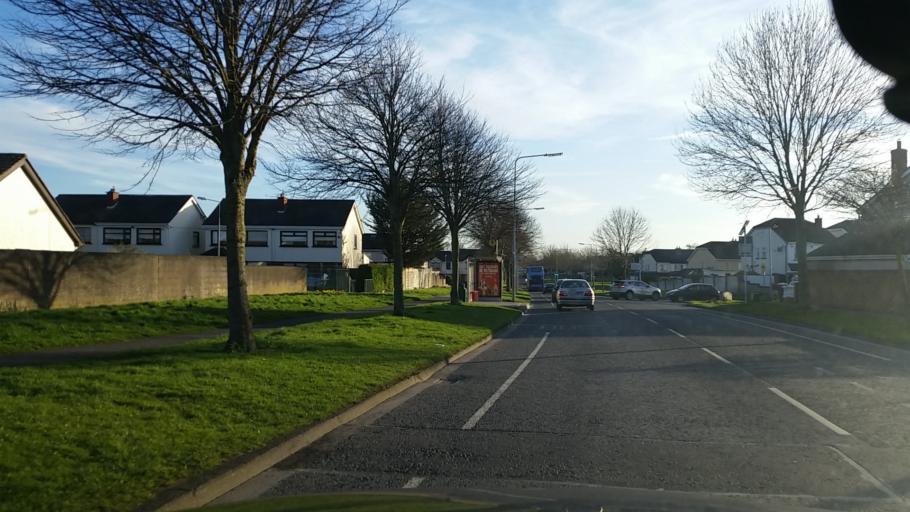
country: IE
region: Leinster
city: Hartstown
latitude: 53.4006
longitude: -6.4132
